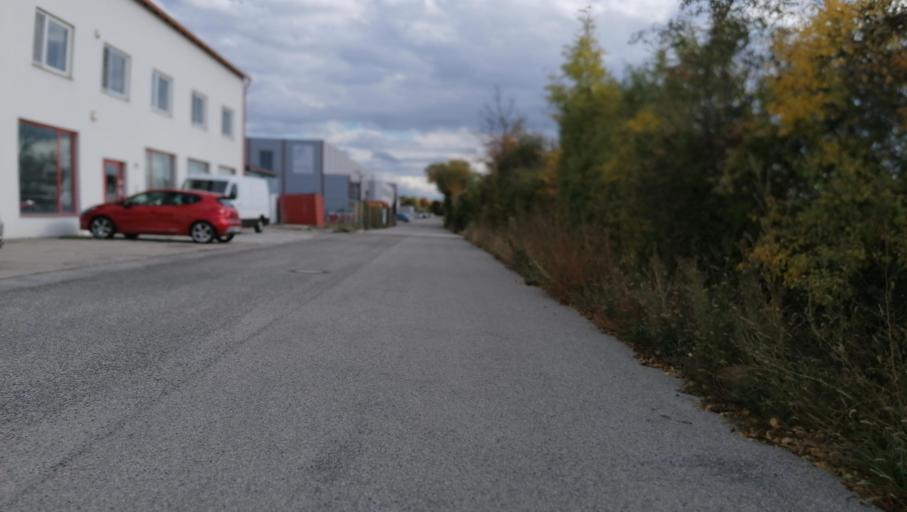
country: AT
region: Lower Austria
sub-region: Politischer Bezirk Baden
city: Tattendorf
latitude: 47.9494
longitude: 16.3107
